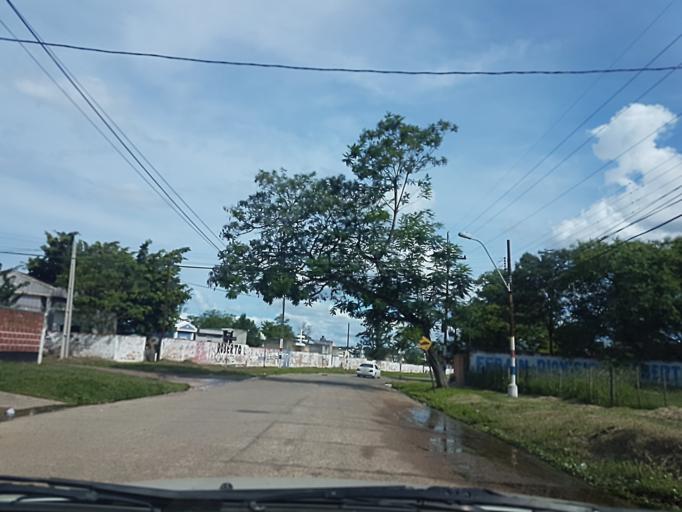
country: PY
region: Central
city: Colonia Mariano Roque Alonso
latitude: -25.2005
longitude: -57.5333
